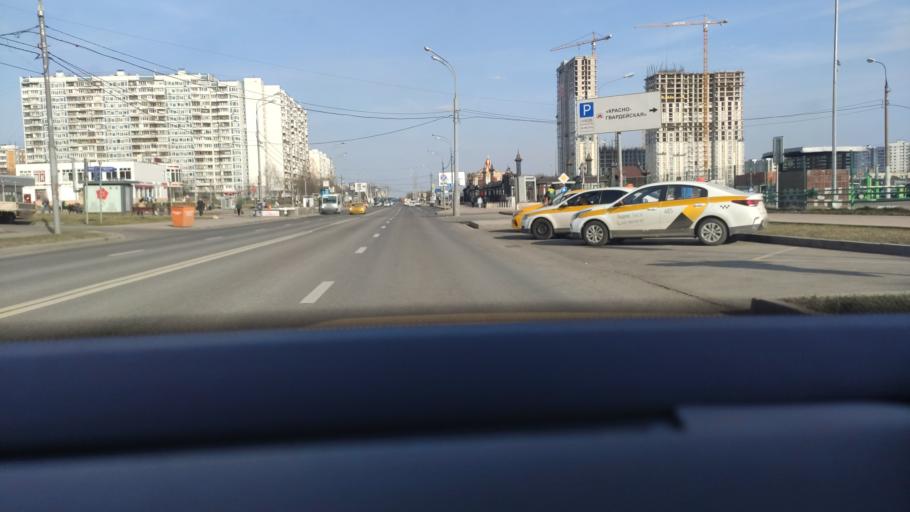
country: RU
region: Moscow
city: Orekhovo-Borisovo
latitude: 55.6137
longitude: 37.7408
